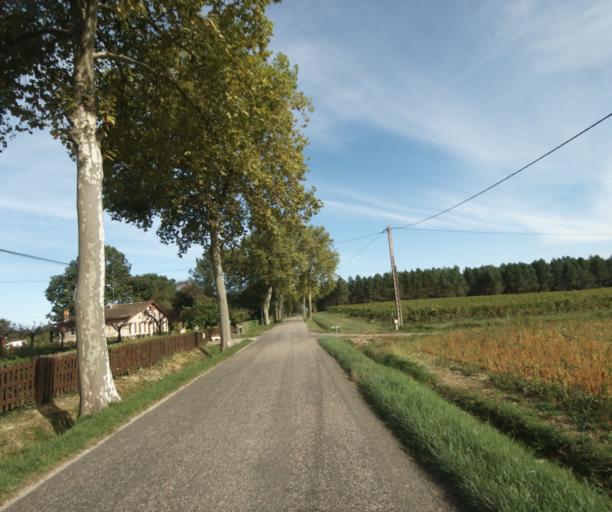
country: FR
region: Midi-Pyrenees
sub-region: Departement du Gers
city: Eauze
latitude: 43.9314
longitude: 0.0919
